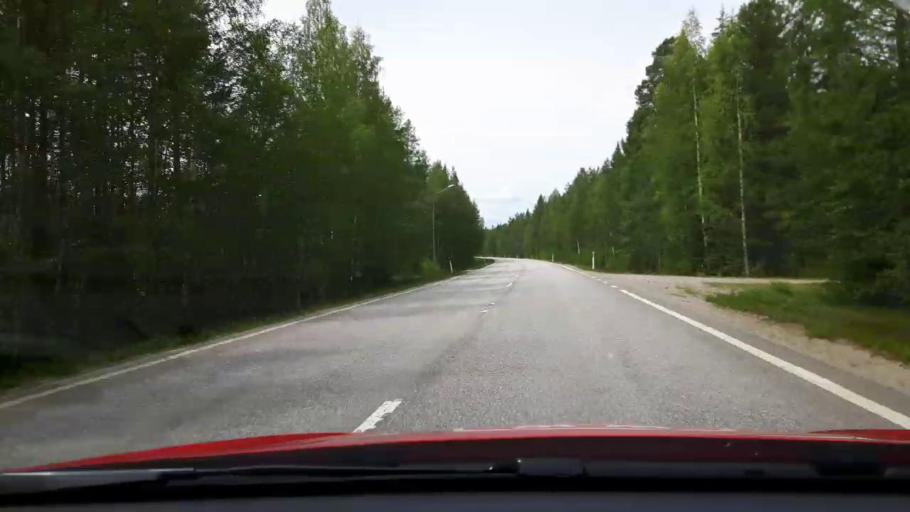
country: SE
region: Jaemtland
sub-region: Harjedalens Kommun
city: Sveg
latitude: 62.1242
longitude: 14.1552
